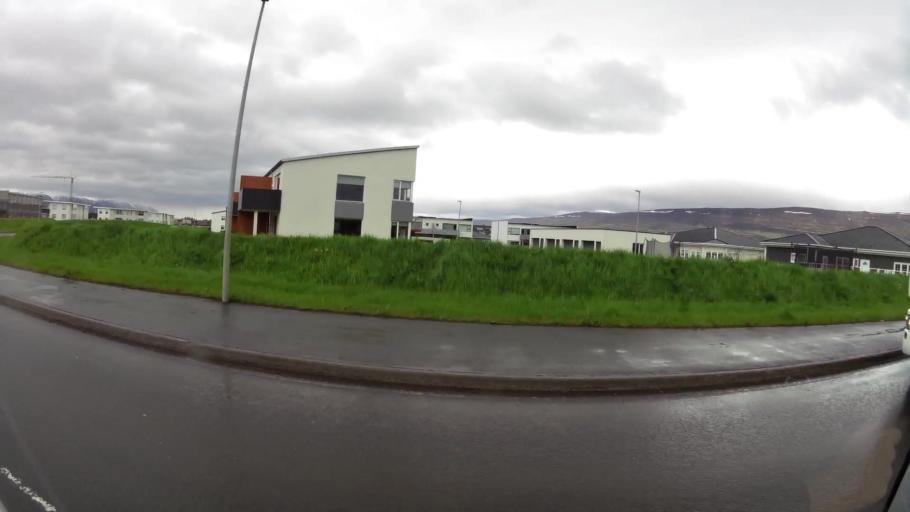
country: IS
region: Northeast
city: Akureyri
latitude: 65.6662
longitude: -18.1067
